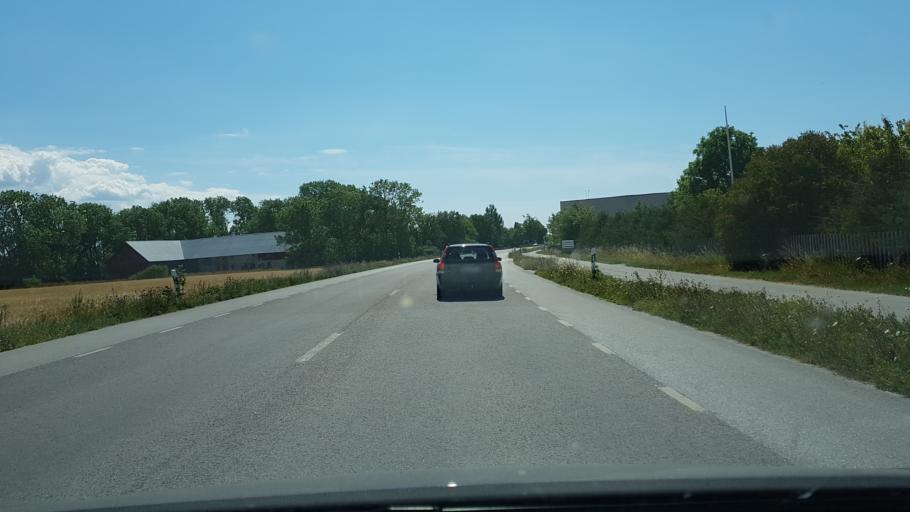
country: SE
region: Gotland
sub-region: Gotland
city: Vibble
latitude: 57.5291
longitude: 18.1764
